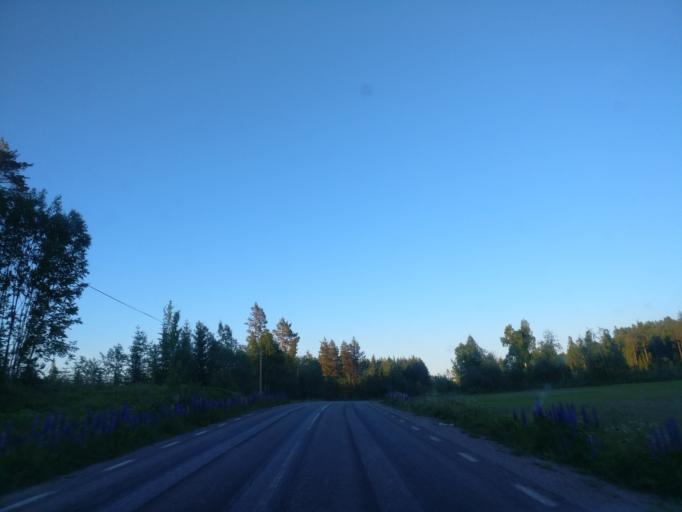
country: SE
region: Vaesternorrland
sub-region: Sundsvalls Kommun
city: Matfors
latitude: 62.2935
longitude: 17.0808
